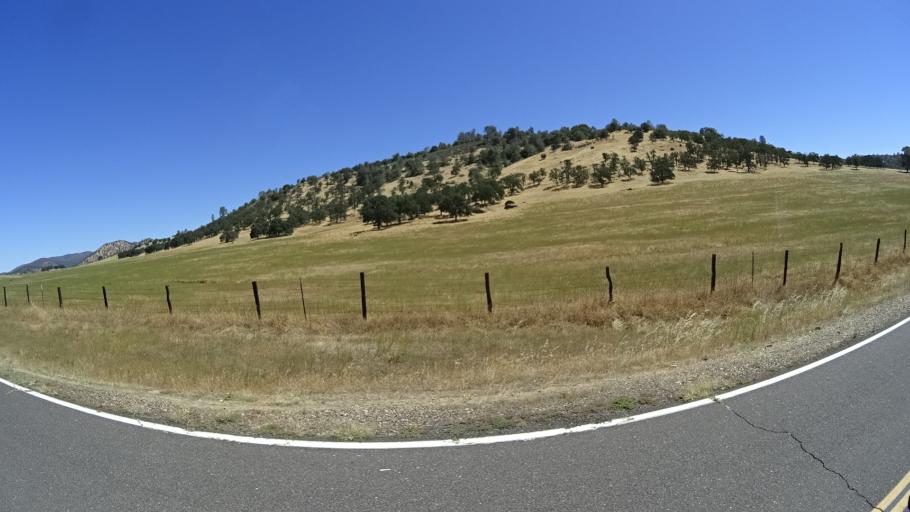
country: US
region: California
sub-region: Calaveras County
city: Copperopolis
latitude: 38.0220
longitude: -120.6859
